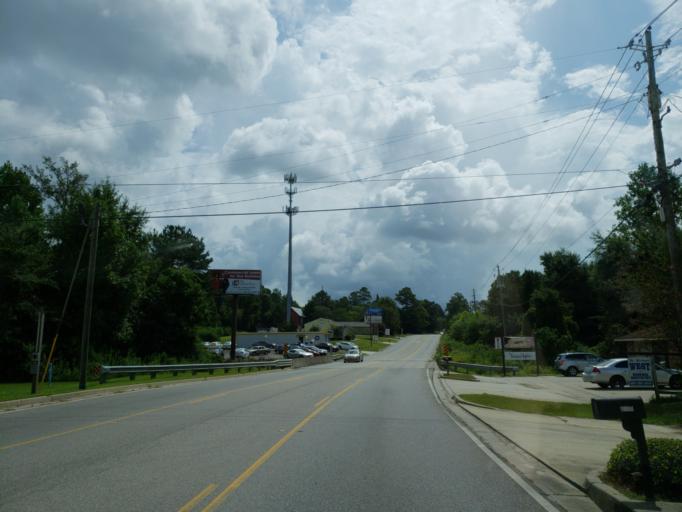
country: US
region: Mississippi
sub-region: Lamar County
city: Arnold Line
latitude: 31.3373
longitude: -89.3552
